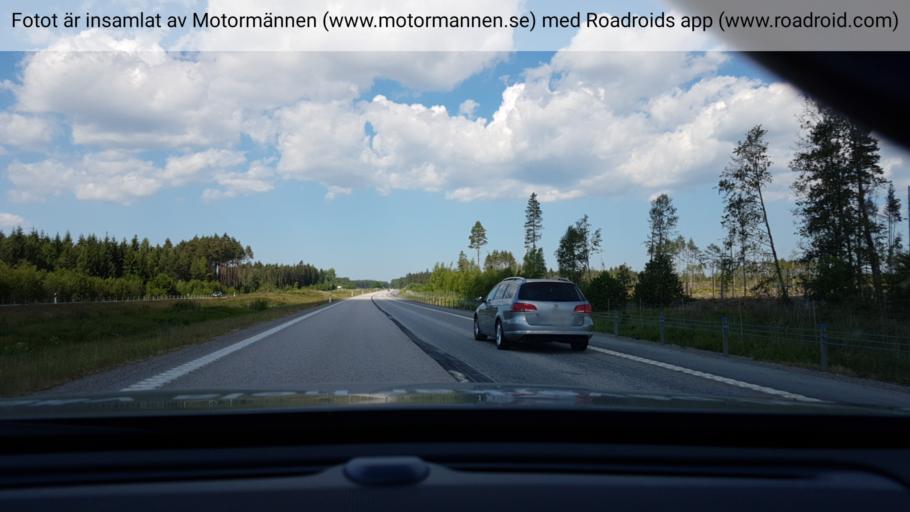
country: SE
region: Uppsala
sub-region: Tierps Kommun
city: Tierp
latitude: 60.2608
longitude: 17.5004
